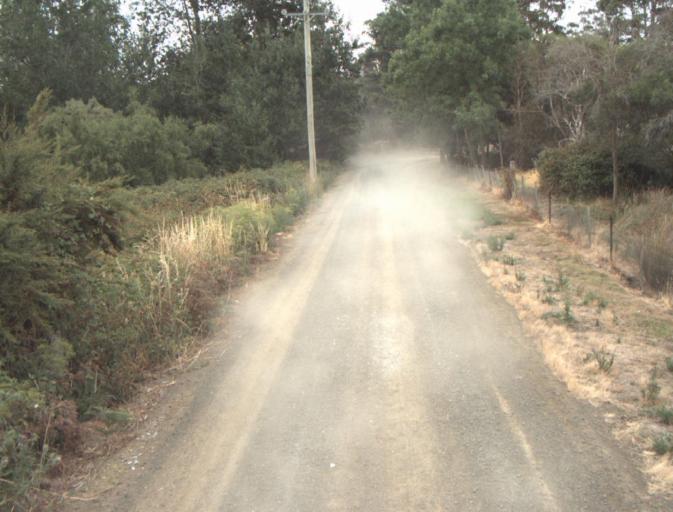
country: AU
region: Tasmania
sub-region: Launceston
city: Mayfield
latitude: -41.2721
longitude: 147.1839
